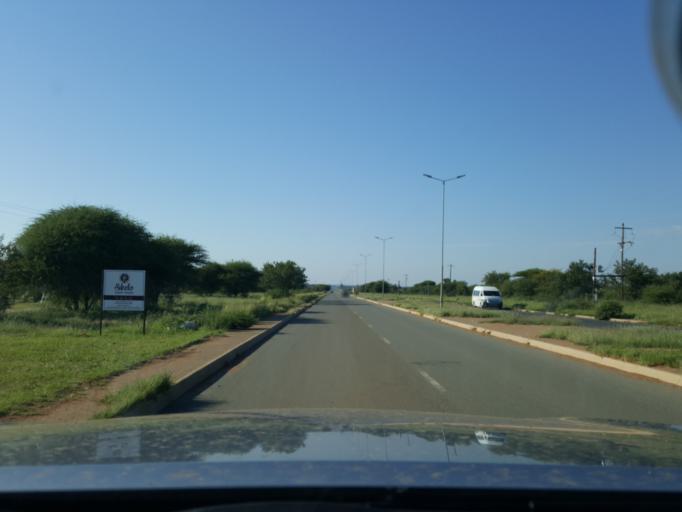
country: ZA
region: North-West
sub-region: Ngaka Modiri Molema District Municipality
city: Mmabatho
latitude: -25.7932
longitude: 25.6302
